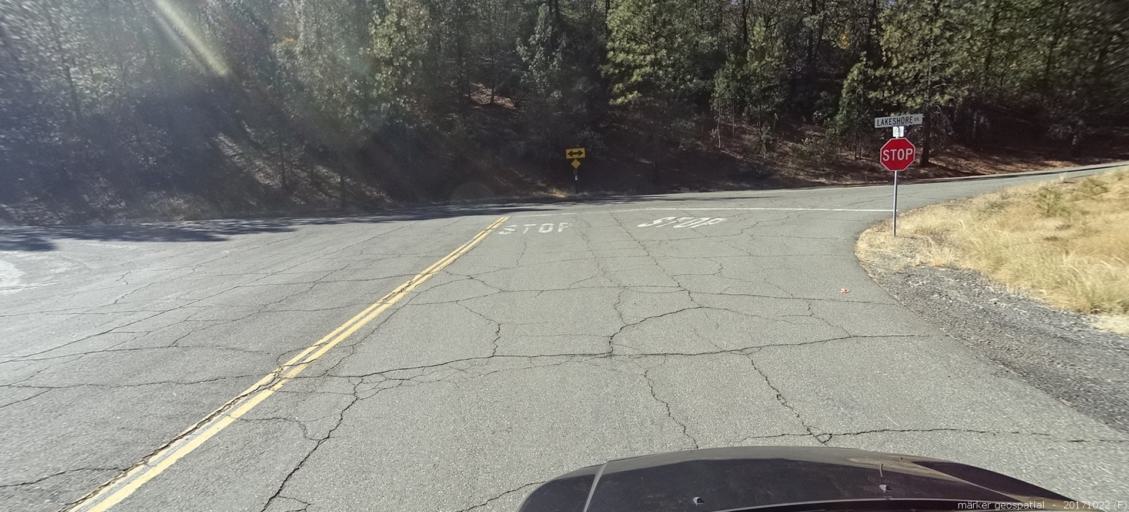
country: US
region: California
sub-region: Shasta County
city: Central Valley (historical)
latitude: 40.9102
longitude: -122.3868
